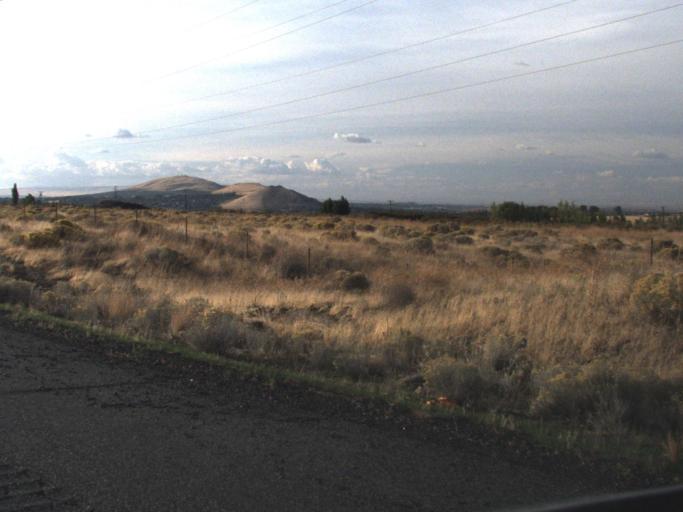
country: US
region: Washington
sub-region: Franklin County
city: West Pasco
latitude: 46.1747
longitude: -119.2190
